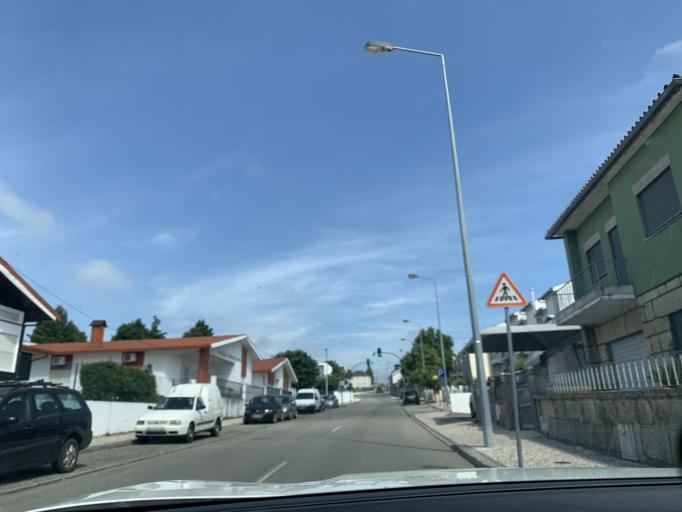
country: PT
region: Viseu
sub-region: Viseu
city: Viseu
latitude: 40.6440
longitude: -7.9037
